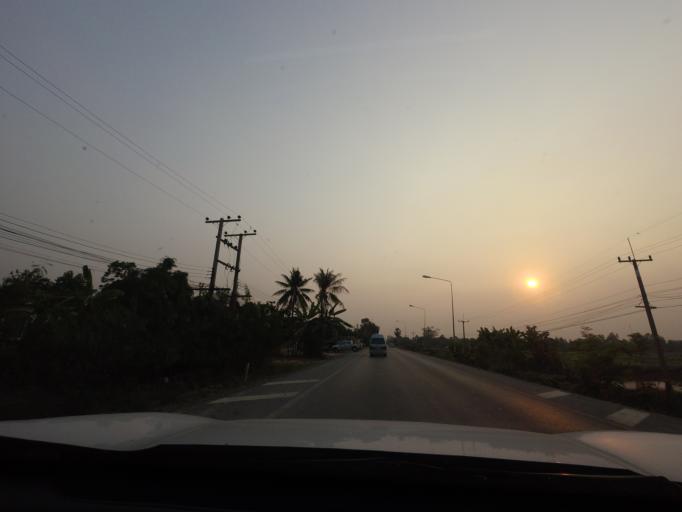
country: TH
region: Nakhon Nayok
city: Ban Na
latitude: 14.1891
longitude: 101.0710
